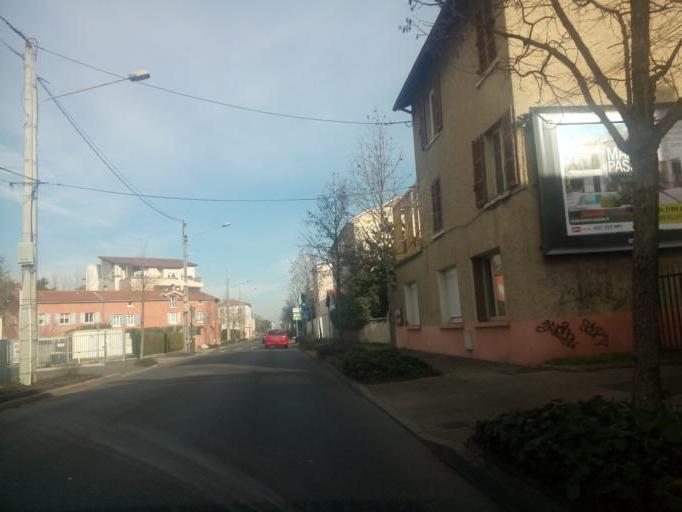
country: FR
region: Rhone-Alpes
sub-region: Departement du Rhone
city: Tassin-la-Demi-Lune
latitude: 45.7564
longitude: 4.7725
